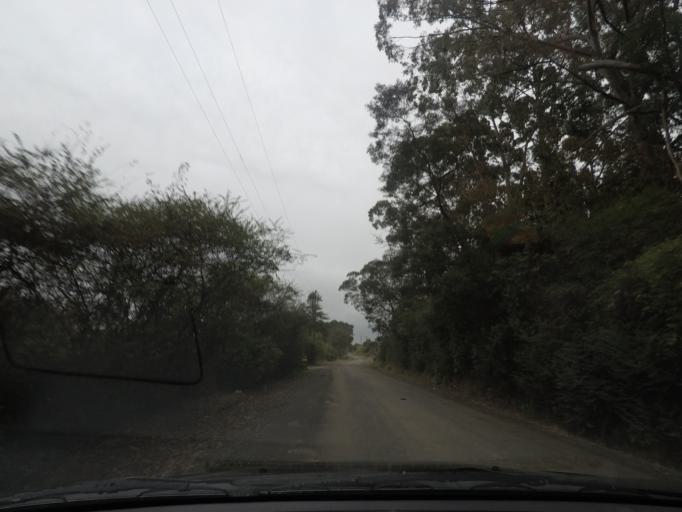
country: NZ
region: Auckland
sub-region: Auckland
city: Muriwai Beach
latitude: -36.7557
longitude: 174.5752
